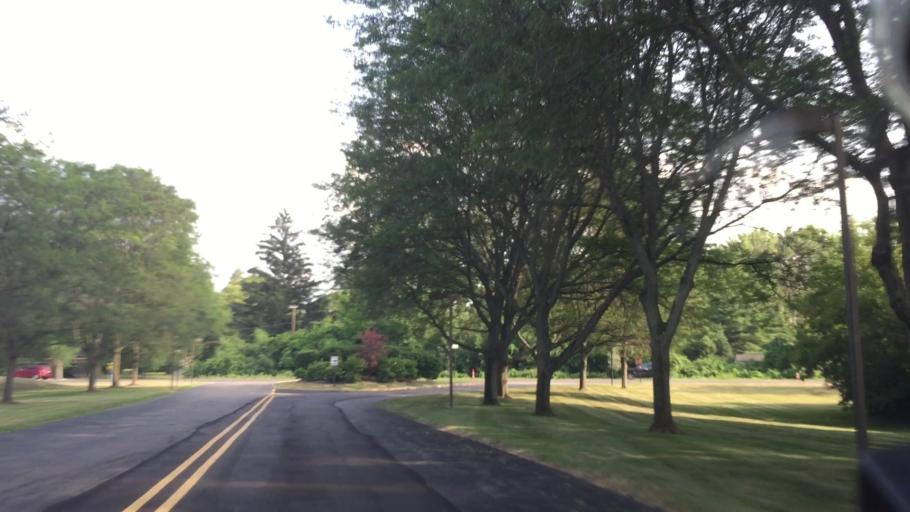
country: US
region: Michigan
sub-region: Oakland County
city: Bingham Farms
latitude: 42.5310
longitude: -83.2872
